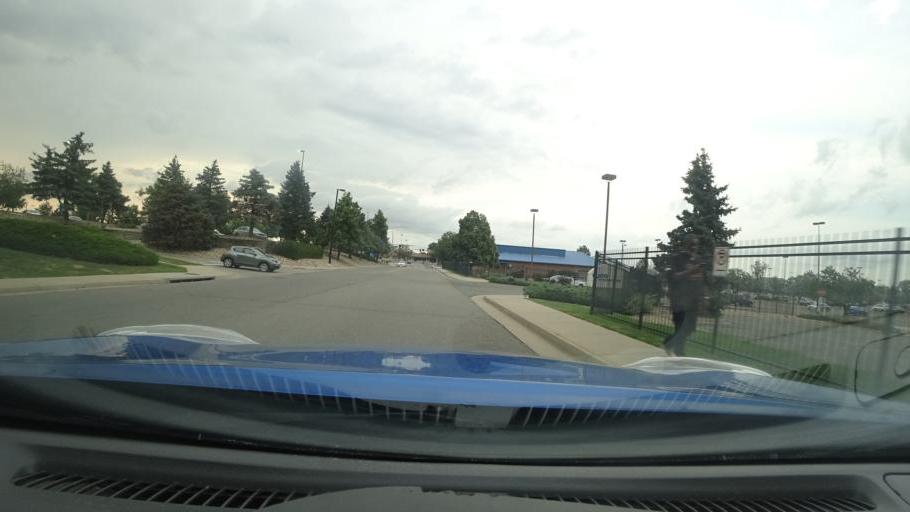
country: US
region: Colorado
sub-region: Adams County
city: Aurora
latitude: 39.7026
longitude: -104.8250
